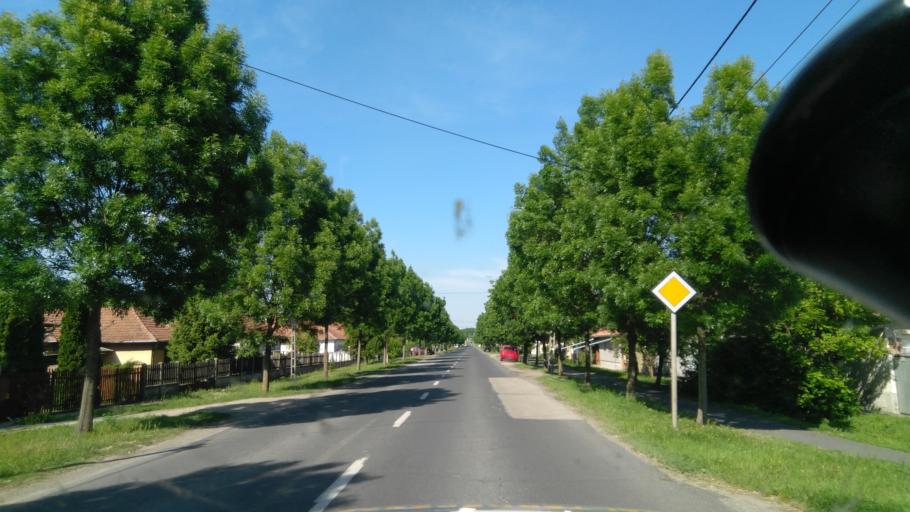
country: HU
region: Bekes
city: Gyula
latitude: 46.6599
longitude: 21.2899
